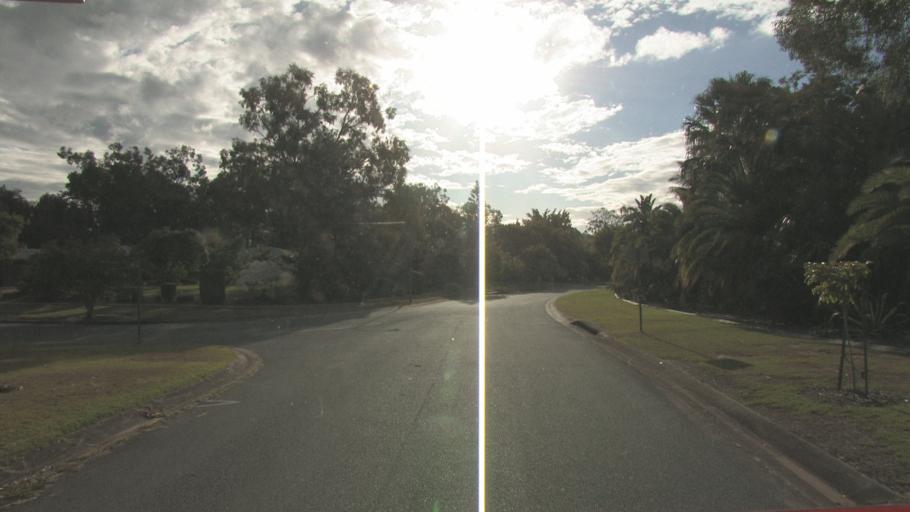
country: AU
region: Queensland
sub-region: Logan
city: Park Ridge South
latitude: -27.7050
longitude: 153.0247
